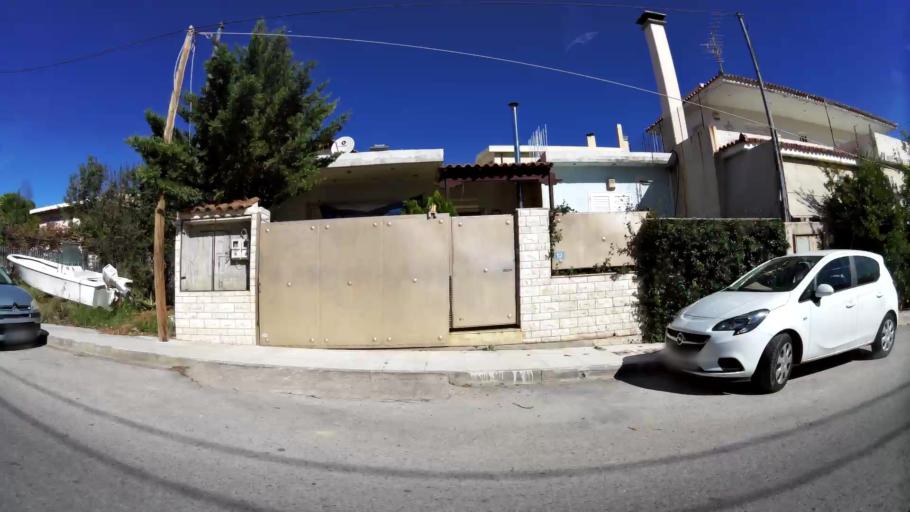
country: GR
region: Attica
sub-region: Nomarchia Anatolikis Attikis
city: Leondarion
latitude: 38.0007
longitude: 23.8531
